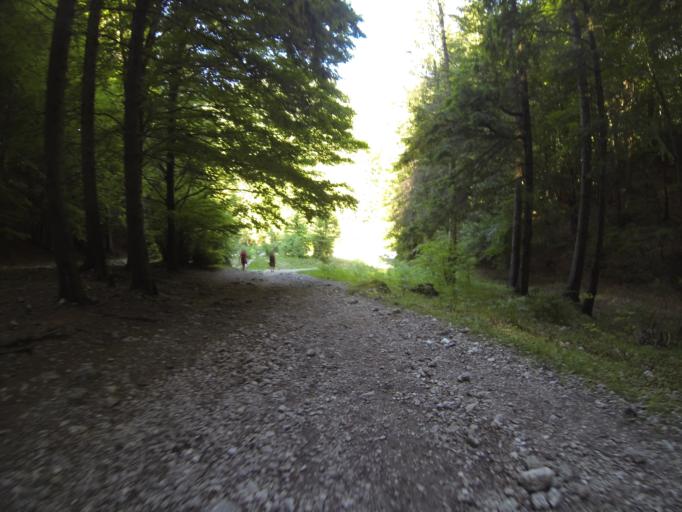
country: RO
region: Brasov
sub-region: Comuna Zarnesti
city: Zarnesti
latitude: 45.5350
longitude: 25.2909
